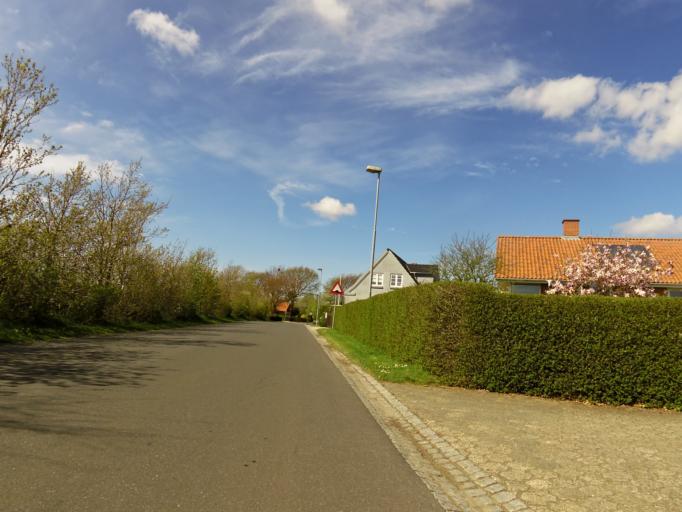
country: DK
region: Central Jutland
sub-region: Skive Kommune
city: Skive
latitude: 56.4674
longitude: 8.9710
